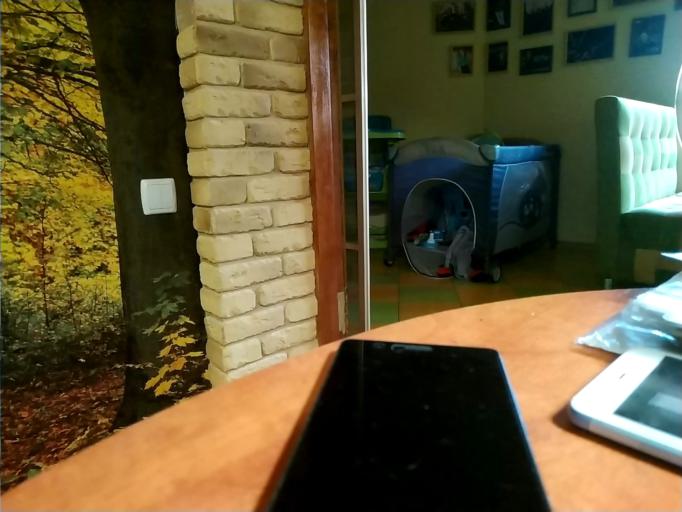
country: RU
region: Kaluga
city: Khvastovichi
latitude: 53.6406
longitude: 35.4540
